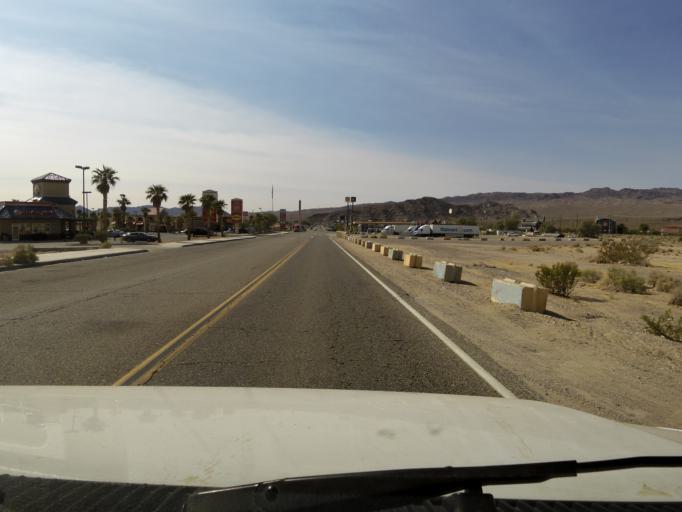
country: US
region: California
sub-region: San Bernardino County
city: Fort Irwin
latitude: 35.2706
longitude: -116.0668
